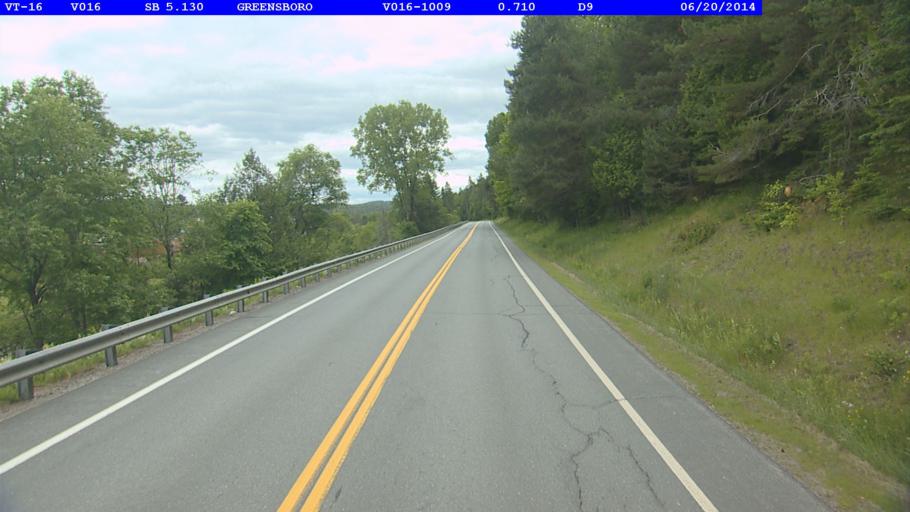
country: US
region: Vermont
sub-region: Caledonia County
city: Hardwick
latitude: 44.5536
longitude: -72.2621
